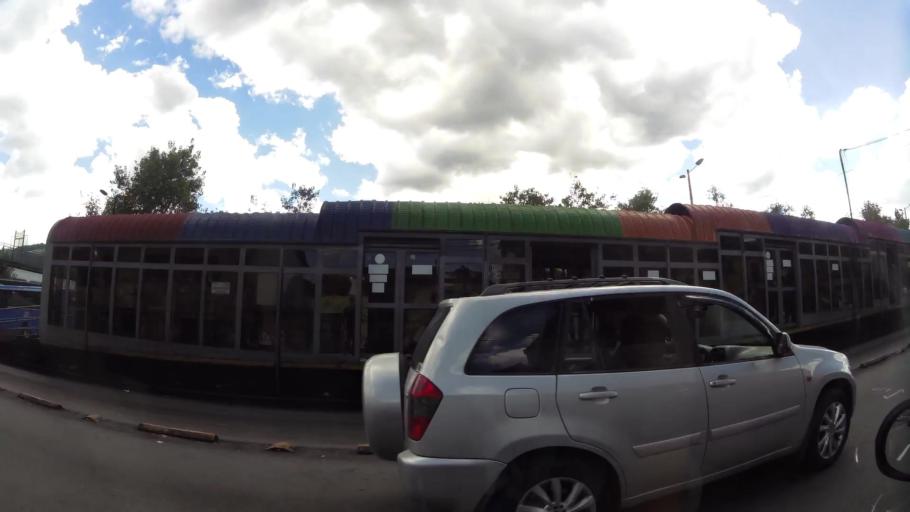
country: EC
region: Pichincha
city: Quito
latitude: -0.1996
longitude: -78.5007
